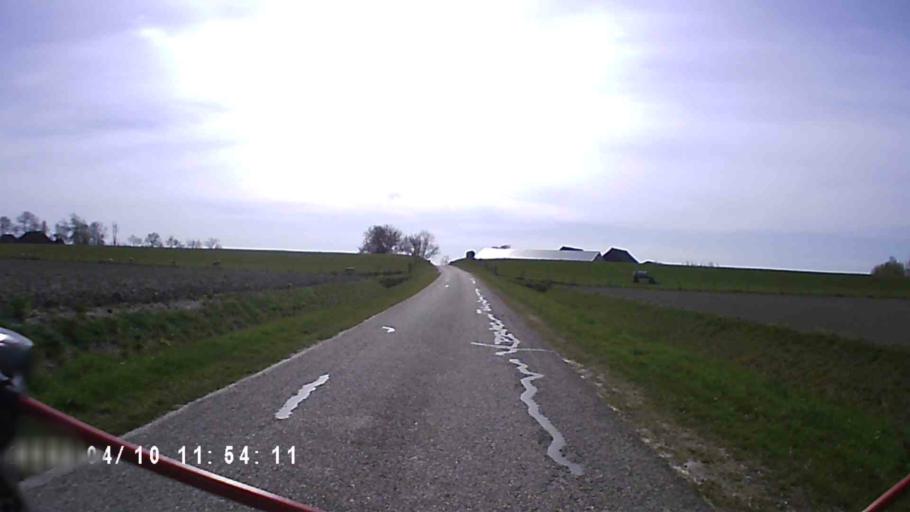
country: NL
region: Groningen
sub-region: Gemeente De Marne
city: Ulrum
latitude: 53.3891
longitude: 6.3302
